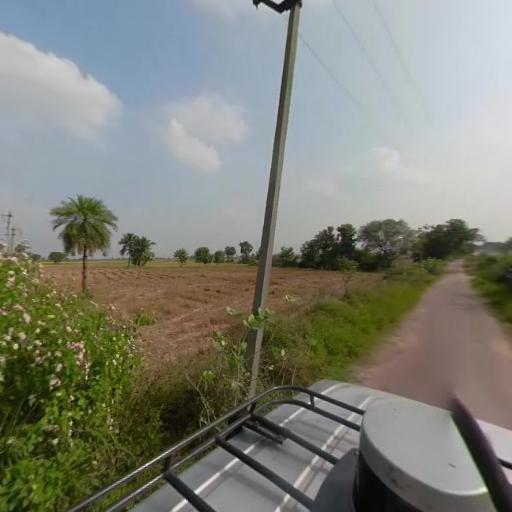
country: IN
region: Telangana
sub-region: Nalgonda
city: Suriapet
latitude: 17.1990
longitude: 79.4906
